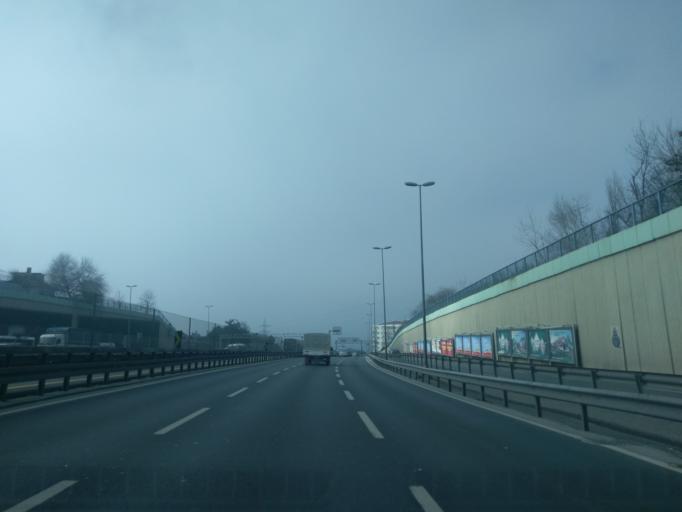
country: TR
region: Istanbul
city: Bahcelievler
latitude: 40.9849
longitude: 28.7795
